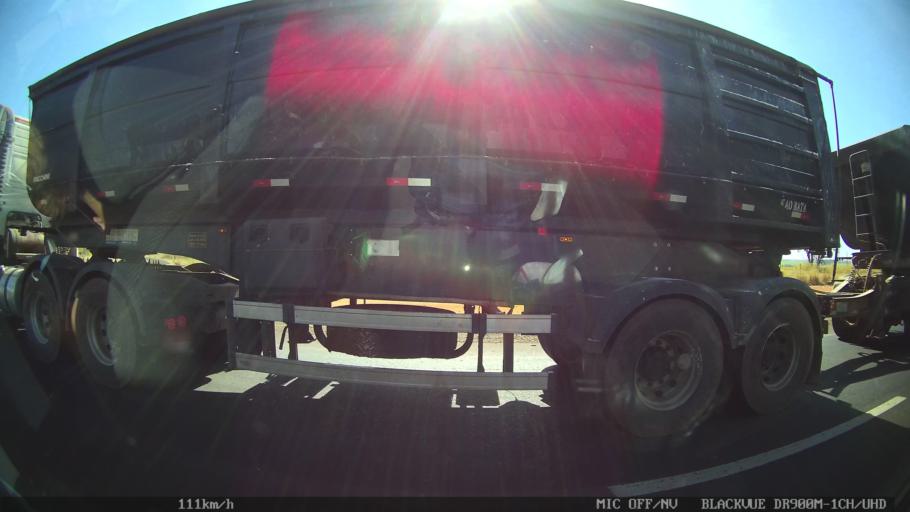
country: BR
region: Sao Paulo
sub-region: Barretos
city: Barretos
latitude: -20.5947
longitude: -48.7155
